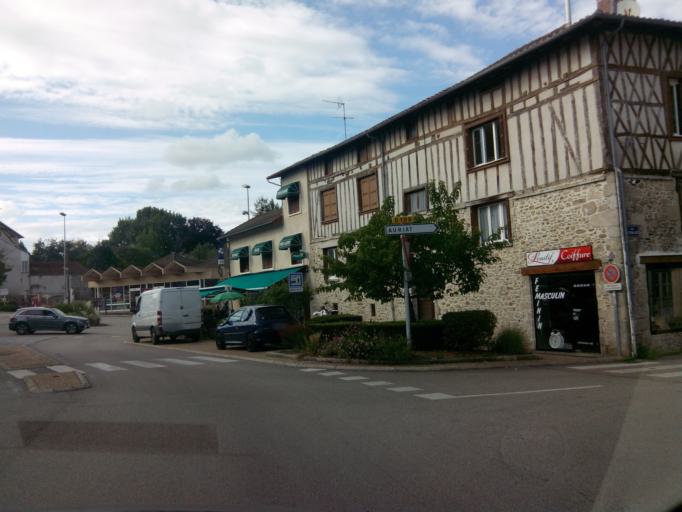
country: FR
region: Limousin
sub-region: Departement de la Haute-Vienne
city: Saint-Leonard-de-Noblat
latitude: 45.8384
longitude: 1.4923
